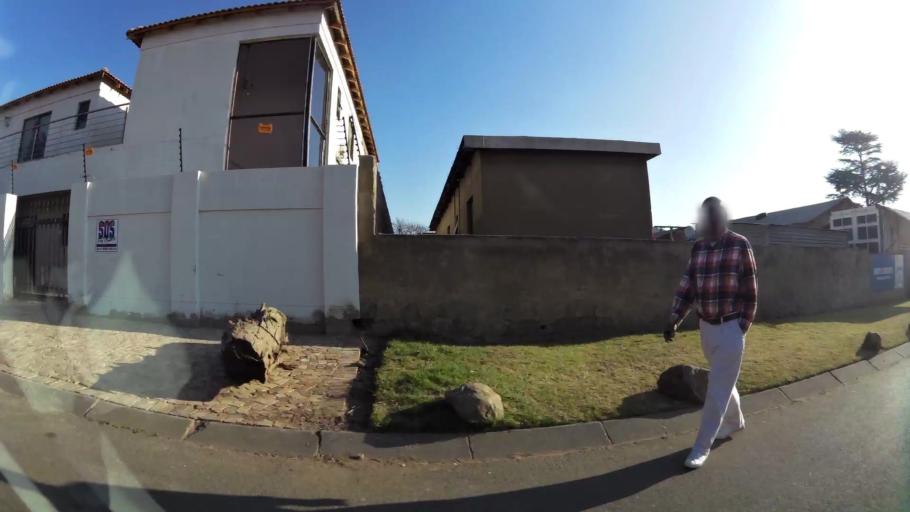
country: ZA
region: Gauteng
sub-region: City of Johannesburg Metropolitan Municipality
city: Soweto
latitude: -26.2647
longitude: 27.8749
